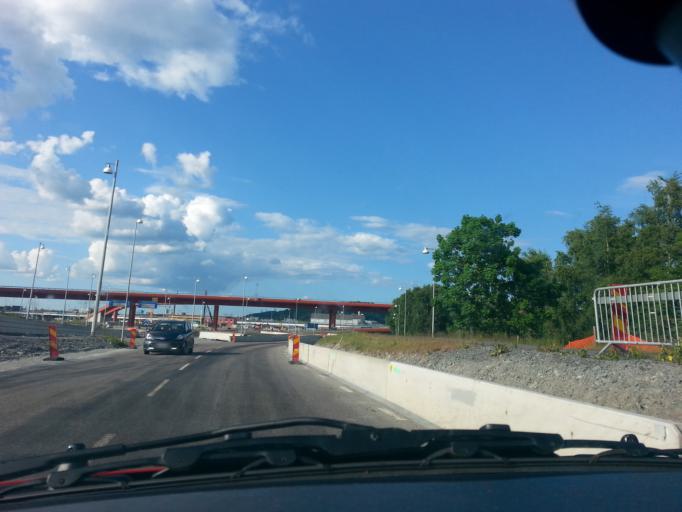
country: SE
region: Vaestra Goetaland
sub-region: Goteborg
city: Goeteborg
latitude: 57.7232
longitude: 11.9978
